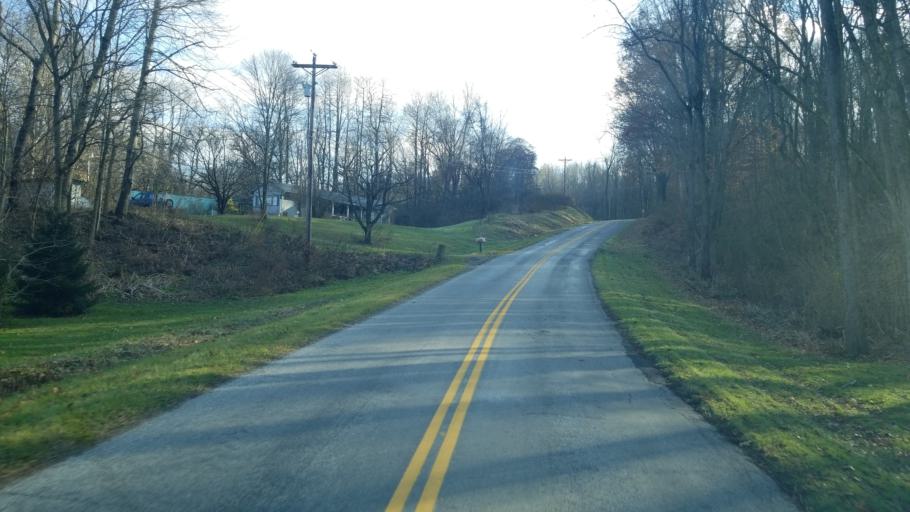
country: US
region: Ohio
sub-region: Ashland County
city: Loudonville
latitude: 40.6659
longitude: -82.3268
